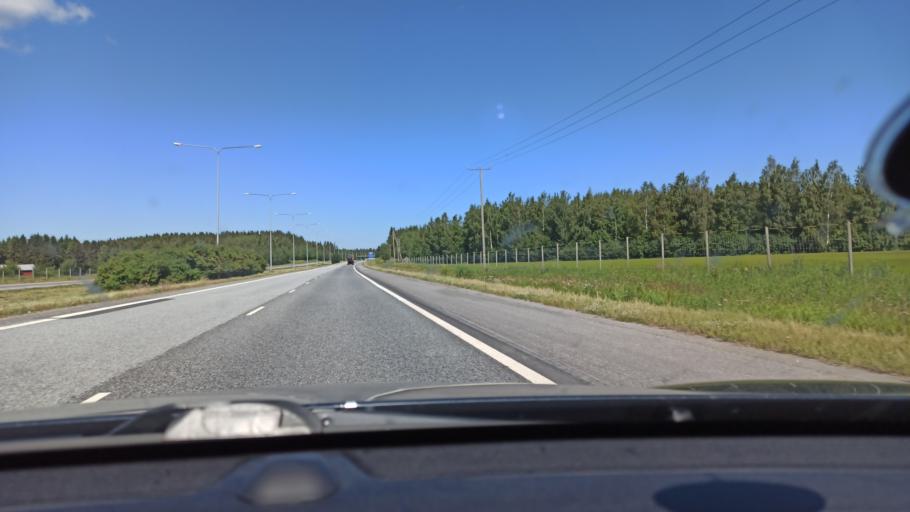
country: FI
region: Ostrobothnia
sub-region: Vaasa
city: Ristinummi
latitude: 63.0460
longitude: 21.7236
